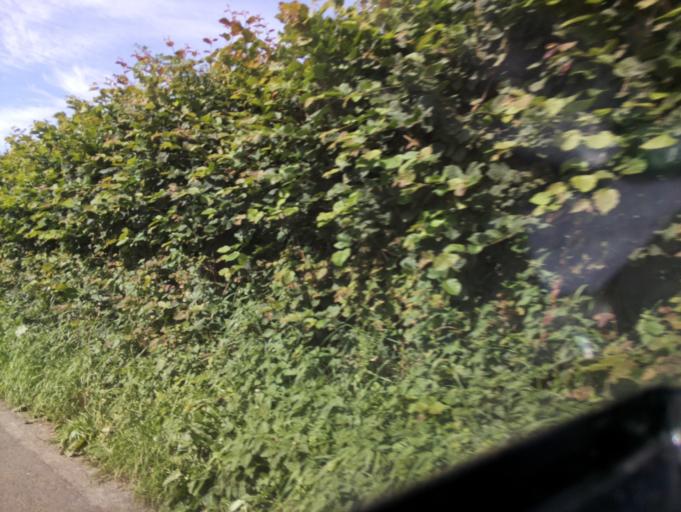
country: GB
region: England
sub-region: Wiltshire
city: Nettleton
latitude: 51.4836
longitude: -2.2667
